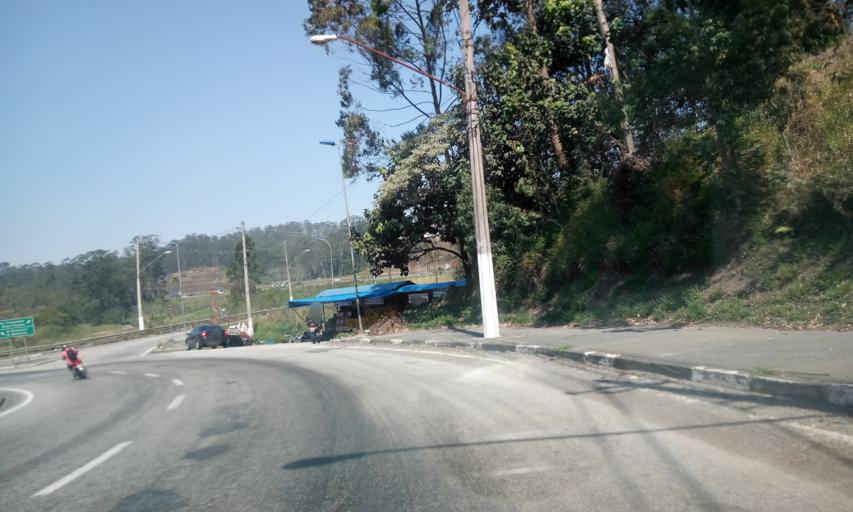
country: BR
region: Sao Paulo
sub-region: Sao Bernardo Do Campo
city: Sao Bernardo do Campo
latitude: -23.7609
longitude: -46.5872
